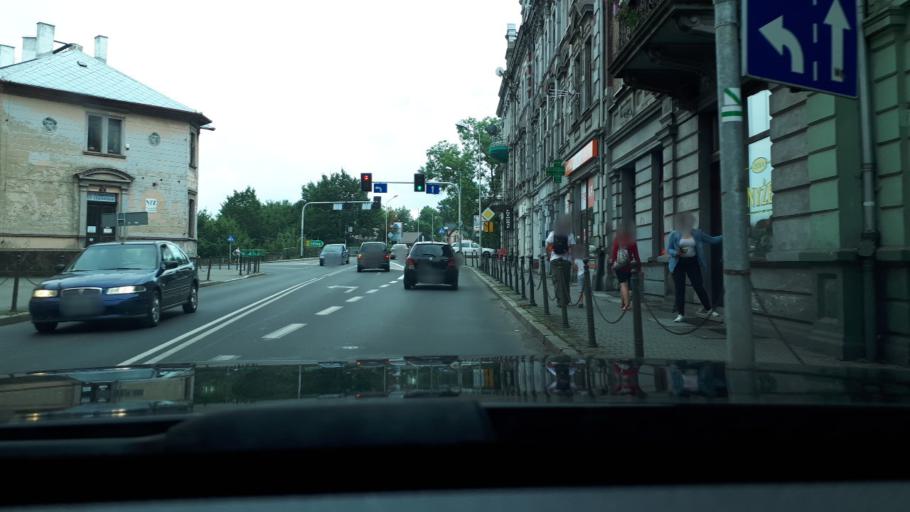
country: PL
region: Lower Silesian Voivodeship
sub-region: Powiat lubanski
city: Luban
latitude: 51.1177
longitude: 15.2894
